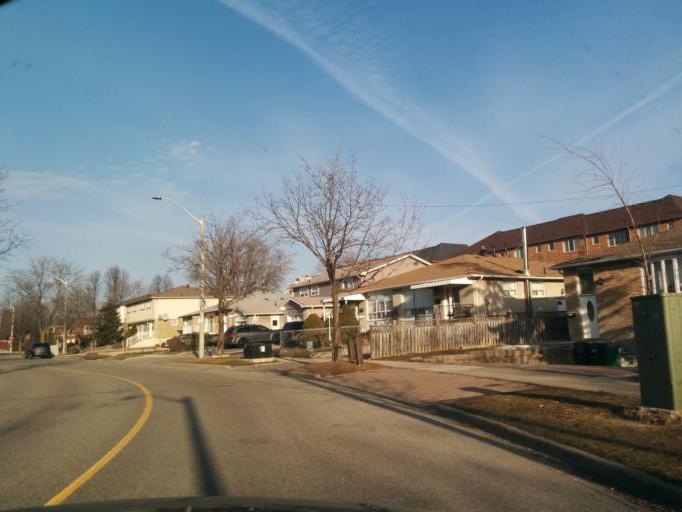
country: CA
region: Ontario
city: Mississauga
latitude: 43.5986
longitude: -79.6002
